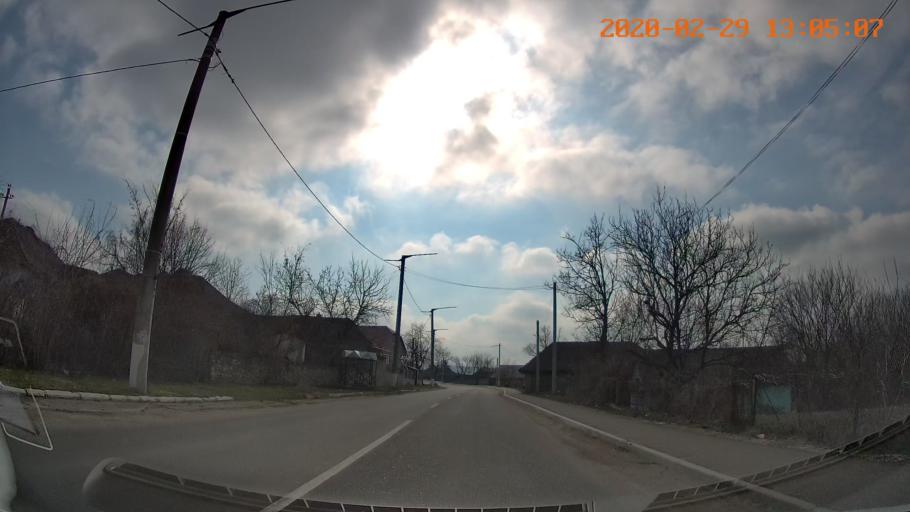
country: MD
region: Telenesti
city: Camenca
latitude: 48.0227
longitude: 28.7082
